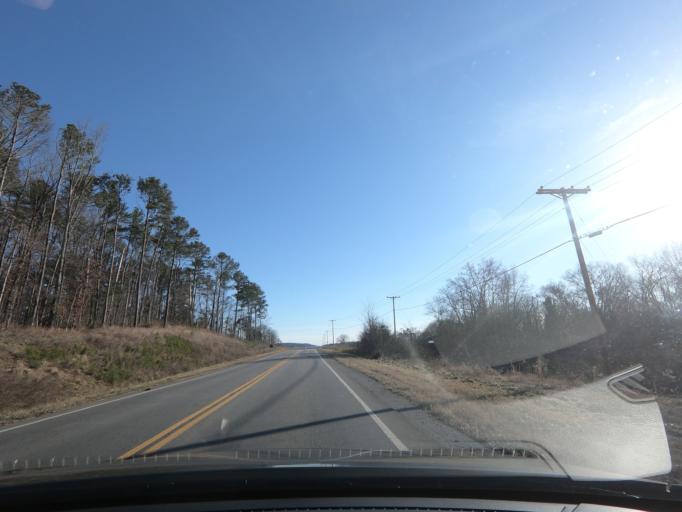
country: US
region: Georgia
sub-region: Gordon County
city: Calhoun
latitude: 34.4479
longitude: -84.9143
